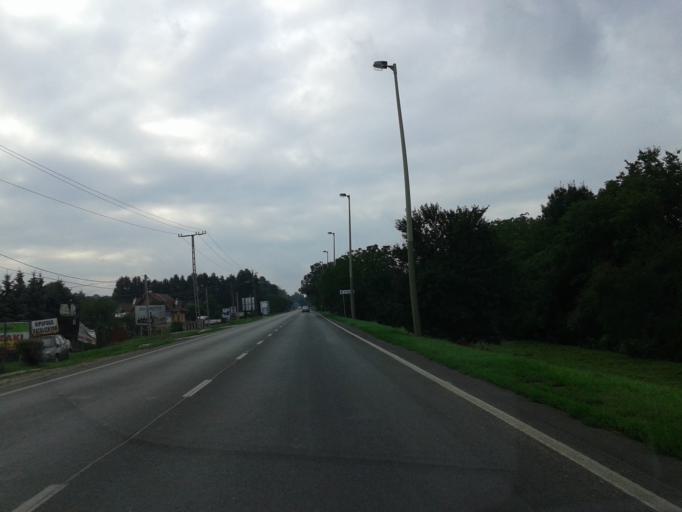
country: HU
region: Csongrad
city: Szeged
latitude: 46.2388
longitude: 20.1676
